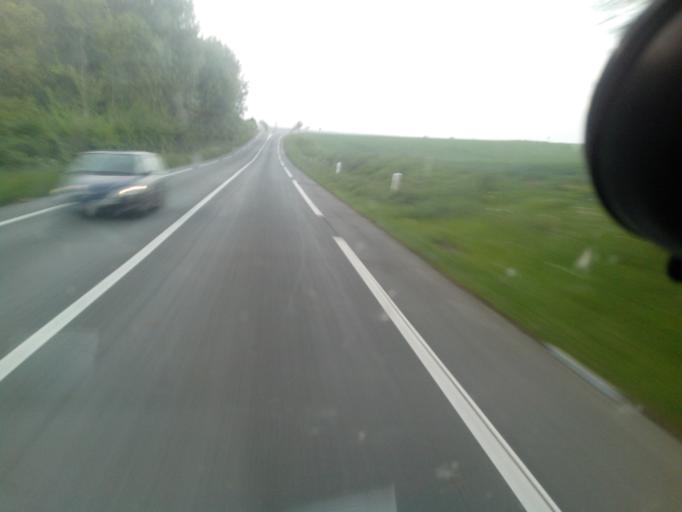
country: FR
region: Nord-Pas-de-Calais
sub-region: Departement du Pas-de-Calais
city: Hesdin
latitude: 50.3494
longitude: 2.0346
